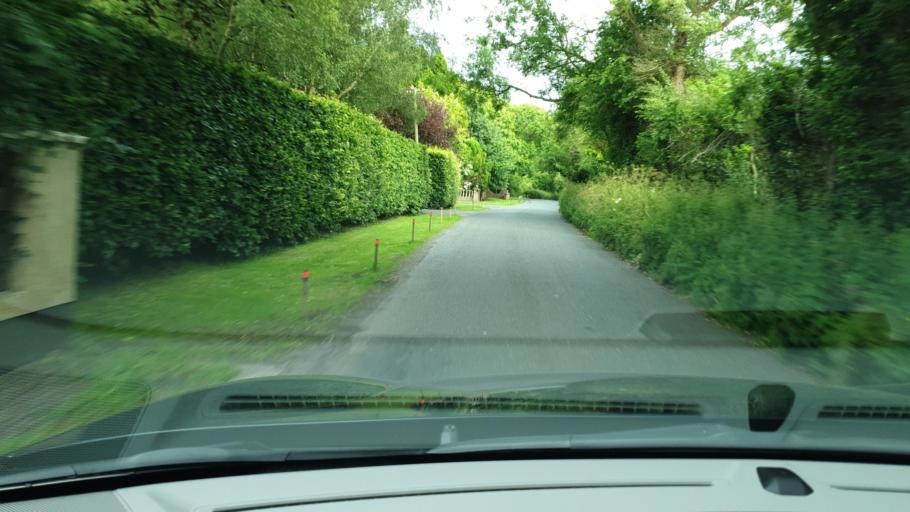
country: IE
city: Confey
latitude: 53.3940
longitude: -6.4973
